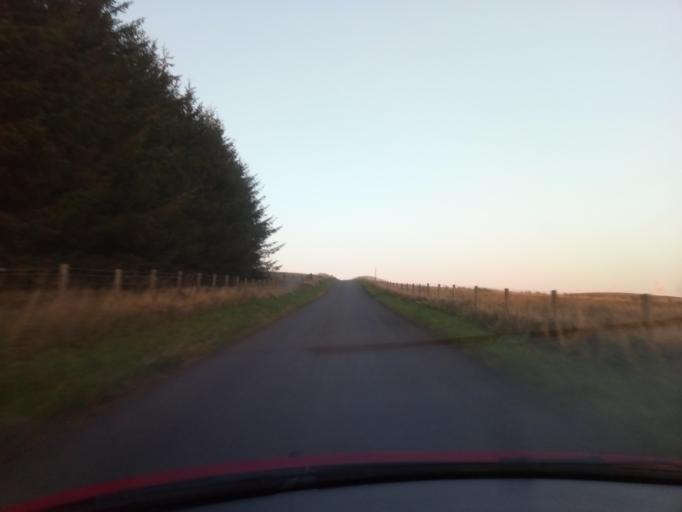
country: GB
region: Scotland
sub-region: East Lothian
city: Pencaitland
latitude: 55.8063
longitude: -2.8865
